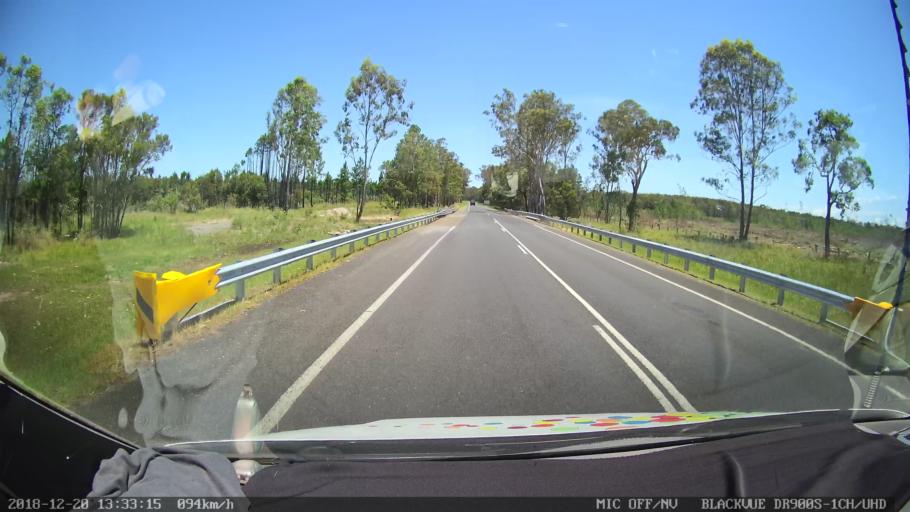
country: AU
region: New South Wales
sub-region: Clarence Valley
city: Gordon
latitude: -29.2428
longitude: 152.9872
